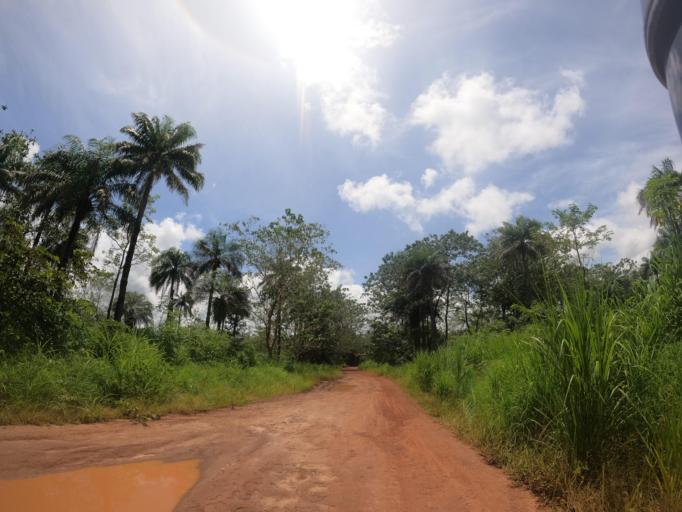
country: SL
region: Northern Province
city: Makeni
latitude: 9.1285
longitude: -12.2620
